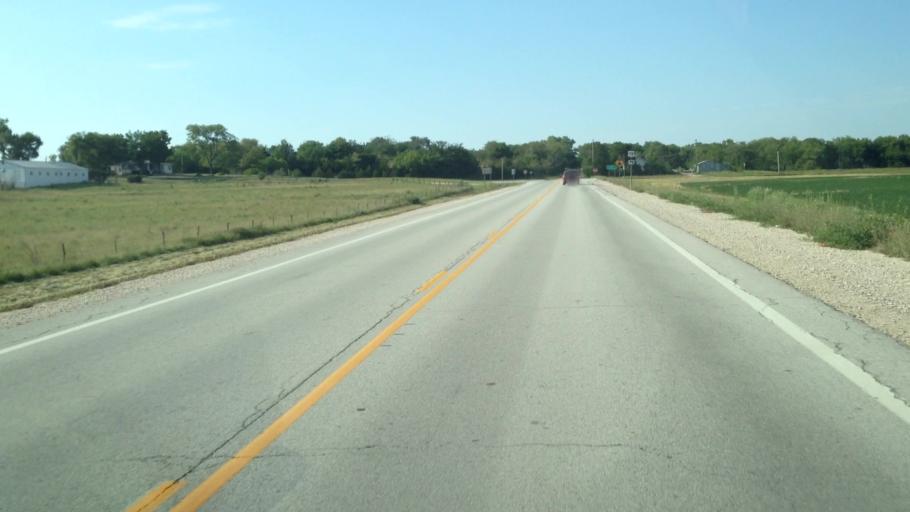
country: US
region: Kansas
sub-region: Anderson County
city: Garnett
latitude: 38.0787
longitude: -95.1694
